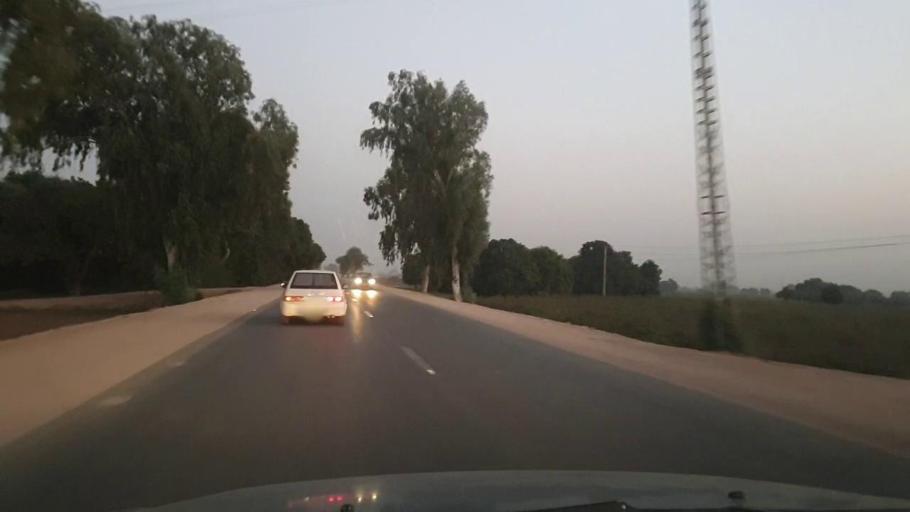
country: PK
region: Sindh
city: Tando Allahyar
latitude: 25.4384
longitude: 68.7394
